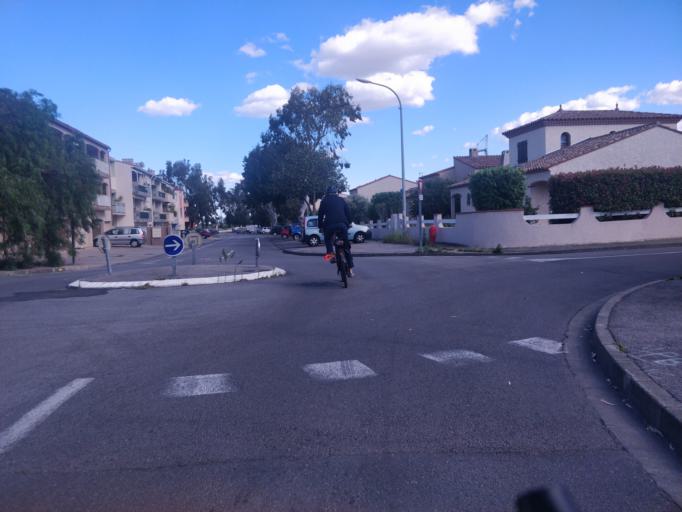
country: FR
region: Languedoc-Roussillon
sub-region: Departement des Pyrenees-Orientales
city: Perpignan
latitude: 42.6837
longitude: 2.9129
